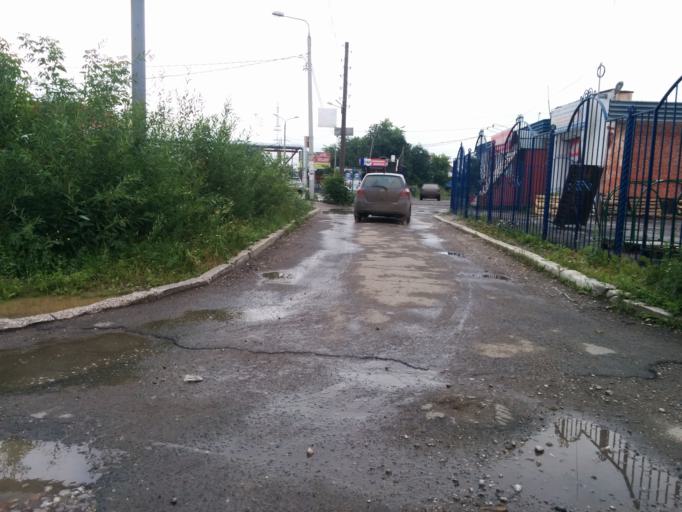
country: RU
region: Perm
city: Perm
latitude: 57.9883
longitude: 56.3021
